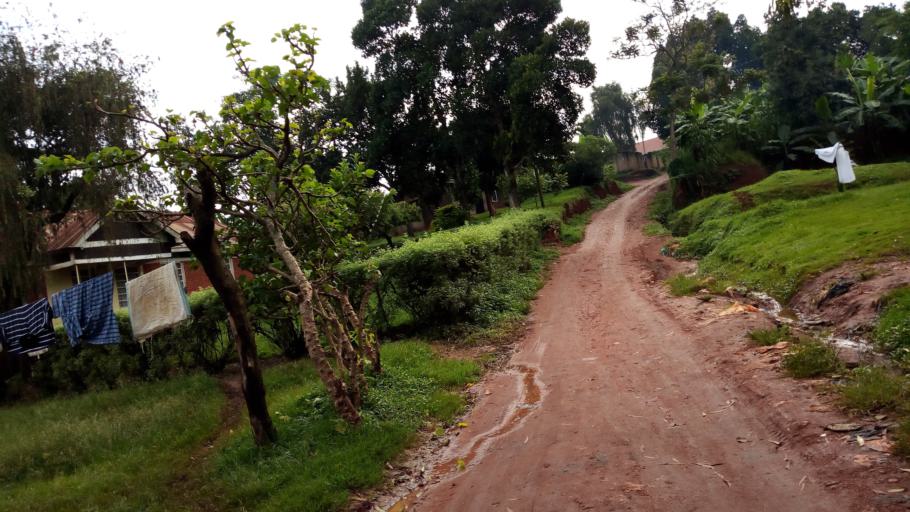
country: UG
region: Central Region
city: Kampala Central Division
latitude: 0.3698
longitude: 32.5566
